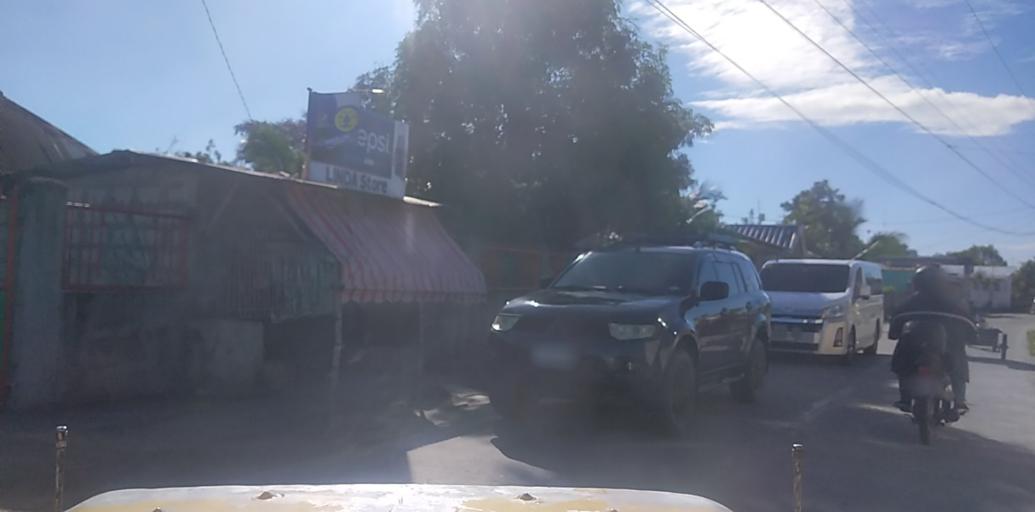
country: PH
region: Central Luzon
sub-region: Province of Pampanga
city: San Patricio
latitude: 15.1118
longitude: 120.7118
